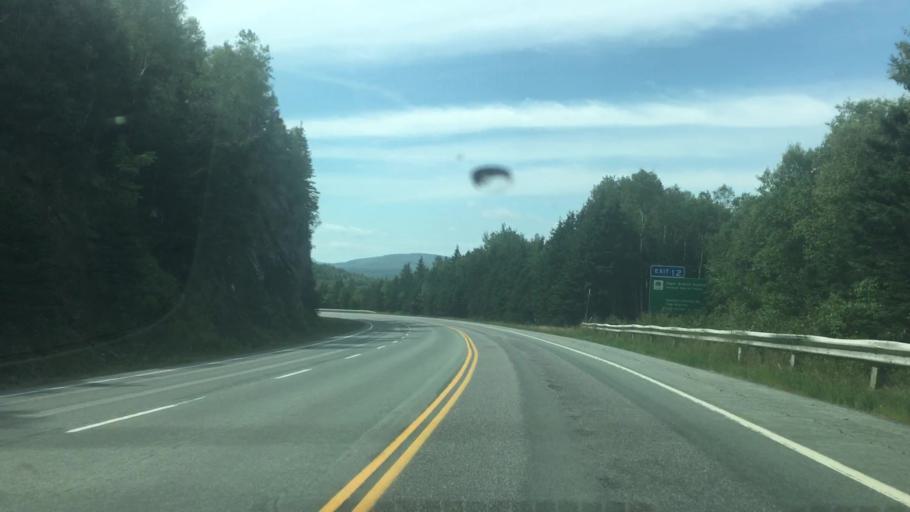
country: CA
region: Nova Scotia
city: Sydney Mines
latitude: 46.2448
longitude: -60.5575
